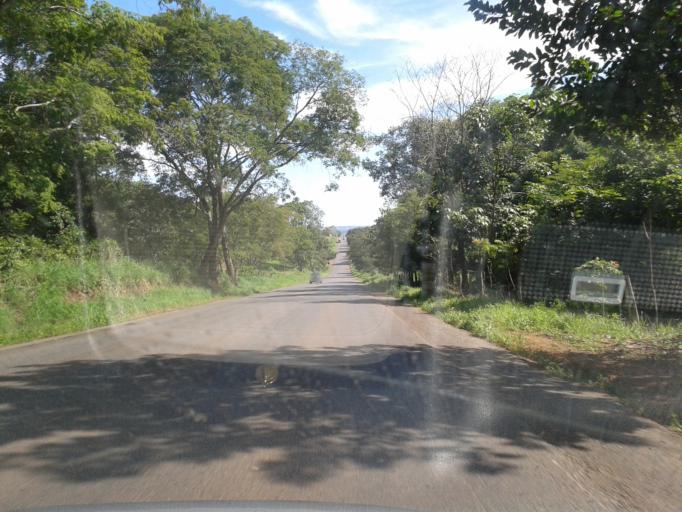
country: BR
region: Goias
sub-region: Piracanjuba
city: Piracanjuba
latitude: -17.2240
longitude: -48.7129
